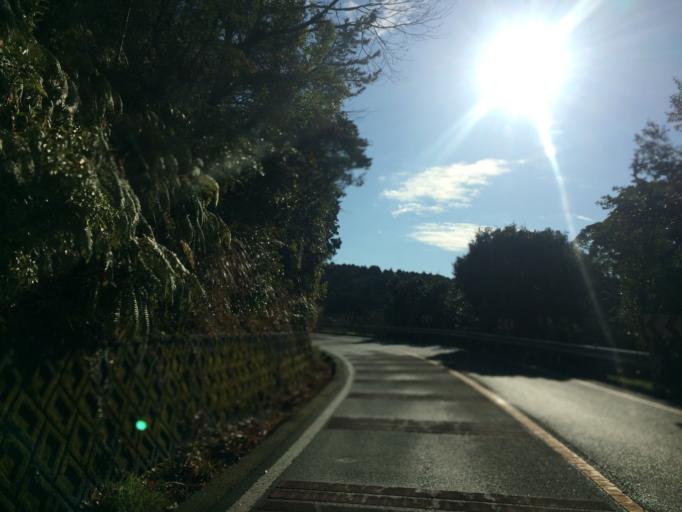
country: JP
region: Shizuoka
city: Shizuoka-shi
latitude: 34.9806
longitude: 138.4404
